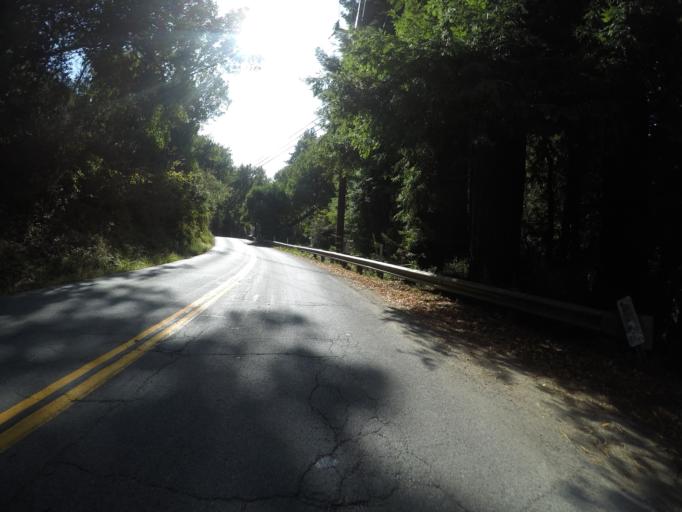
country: US
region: California
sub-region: Santa Cruz County
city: Soquel
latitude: 36.9991
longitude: -121.9705
